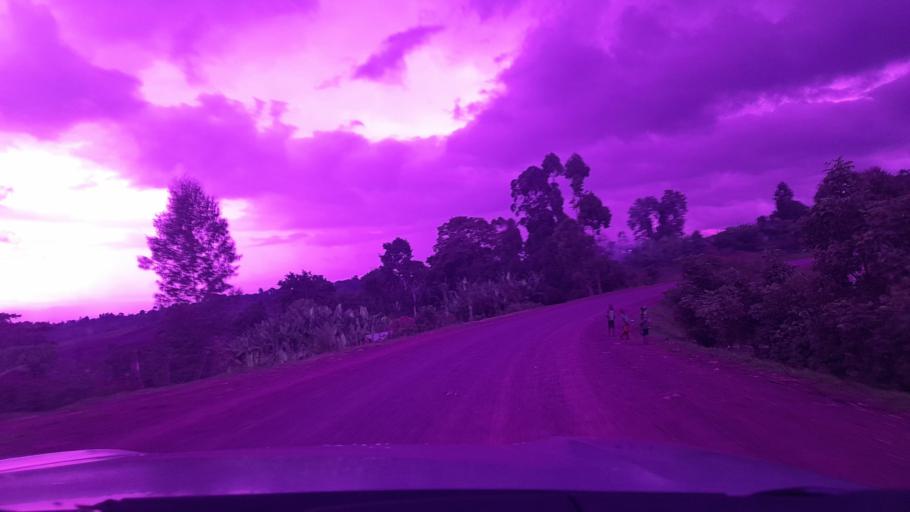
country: ET
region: Southern Nations, Nationalities, and People's Region
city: Mizan Teferi
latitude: 6.9011
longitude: 35.8395
